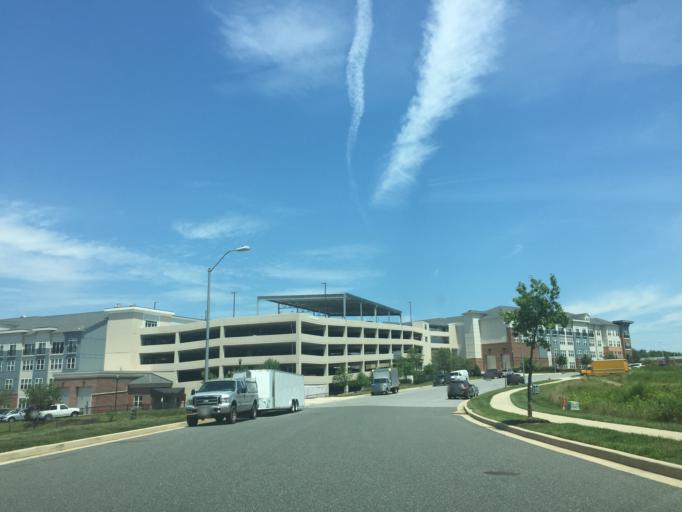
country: US
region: Maryland
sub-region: Baltimore County
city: Bowleys Quarters
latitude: 39.3541
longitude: -76.4128
